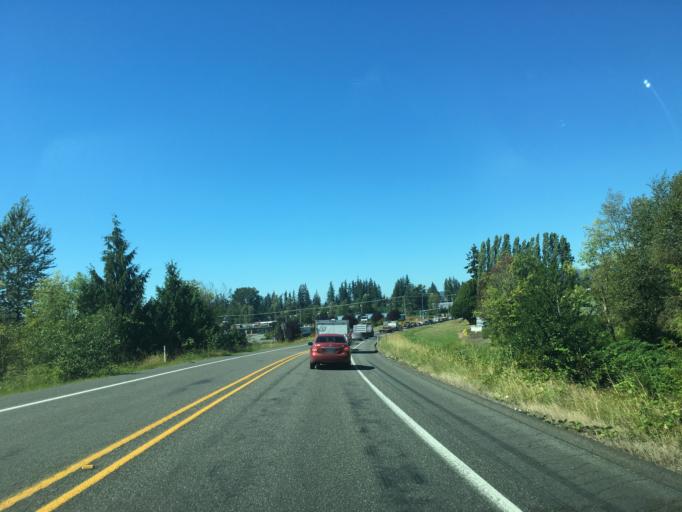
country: US
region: Washington
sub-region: Snohomish County
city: Arlington
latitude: 48.1778
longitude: -122.1283
